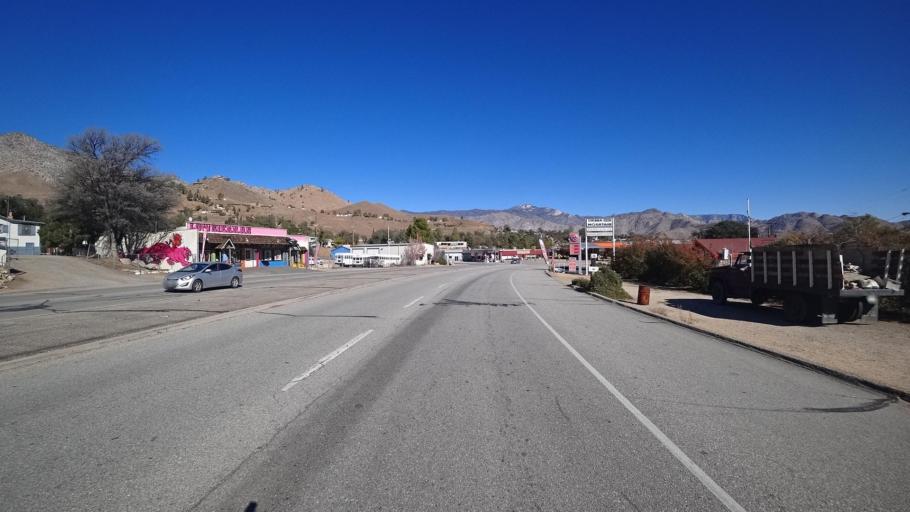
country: US
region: California
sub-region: Kern County
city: Wofford Heights
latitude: 35.7075
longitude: -118.4558
